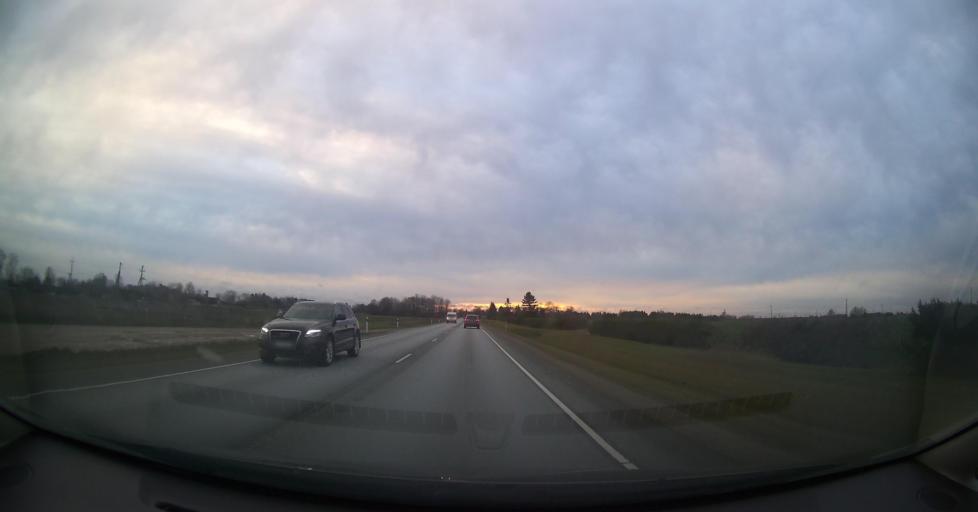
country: EE
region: Ida-Virumaa
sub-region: Puessi linn
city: Pussi
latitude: 59.4079
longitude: 27.1092
